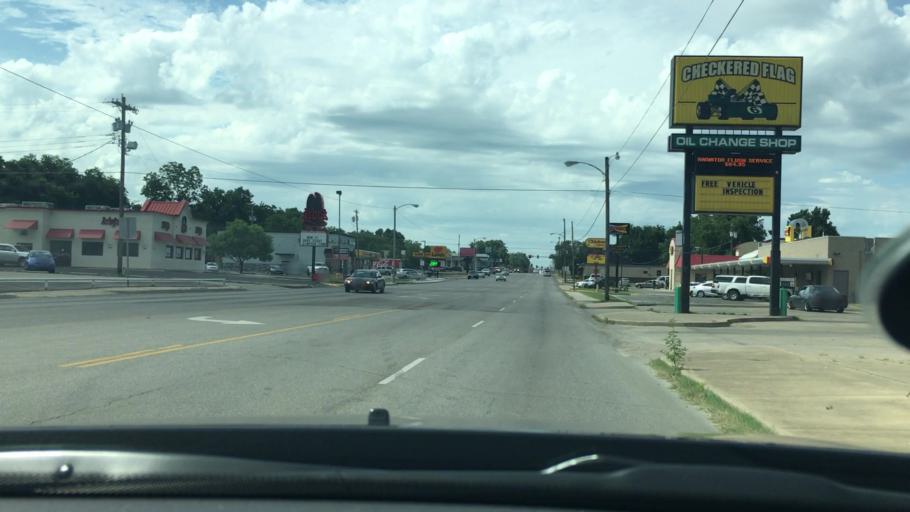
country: US
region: Oklahoma
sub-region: Pontotoc County
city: Ada
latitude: 34.7786
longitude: -96.6700
